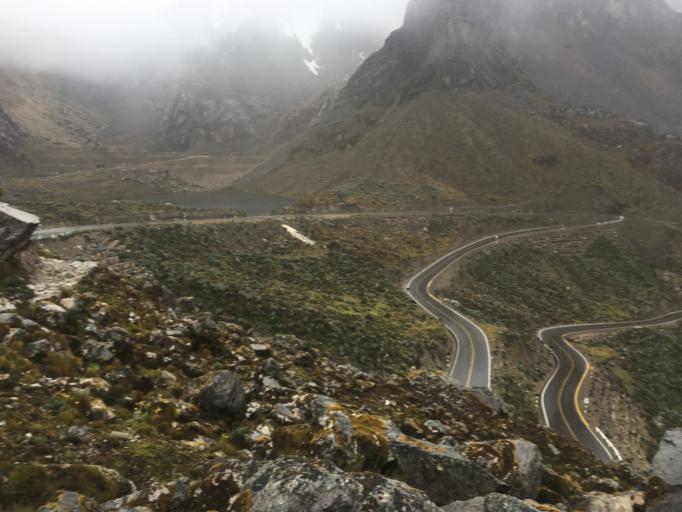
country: PE
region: Ancash
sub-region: Provincia de Yungay
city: Yanama
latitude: -9.1411
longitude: -77.5031
